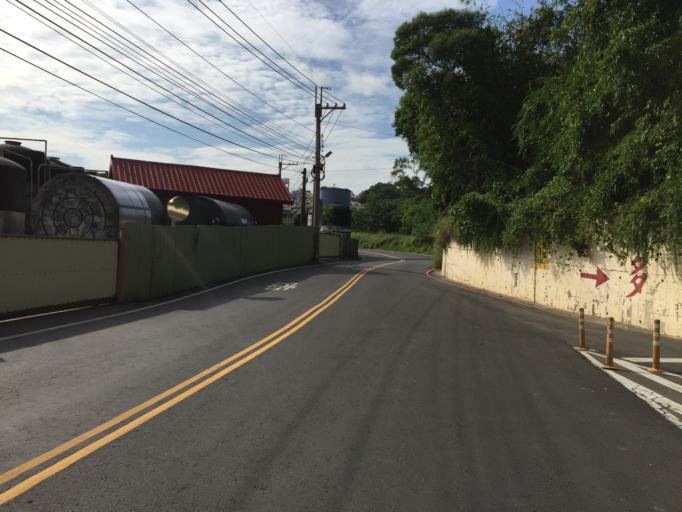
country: TW
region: Taiwan
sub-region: Hsinchu
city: Hsinchu
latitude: 24.7743
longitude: 120.9330
